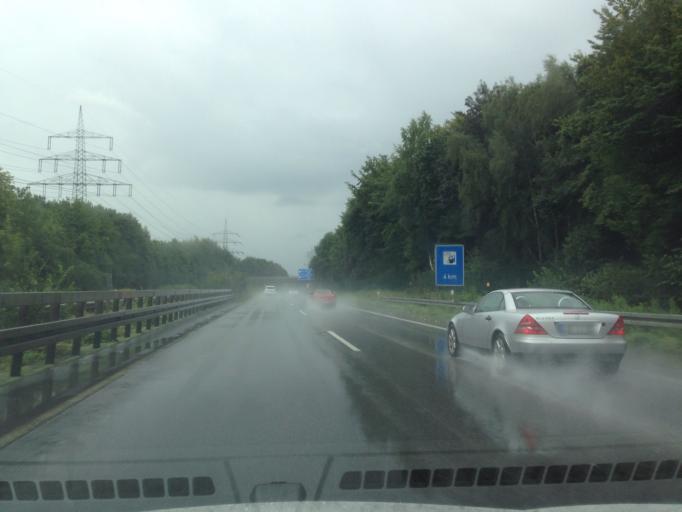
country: DE
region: North Rhine-Westphalia
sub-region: Regierungsbezirk Munster
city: Gladbeck
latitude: 51.6046
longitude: 7.0341
